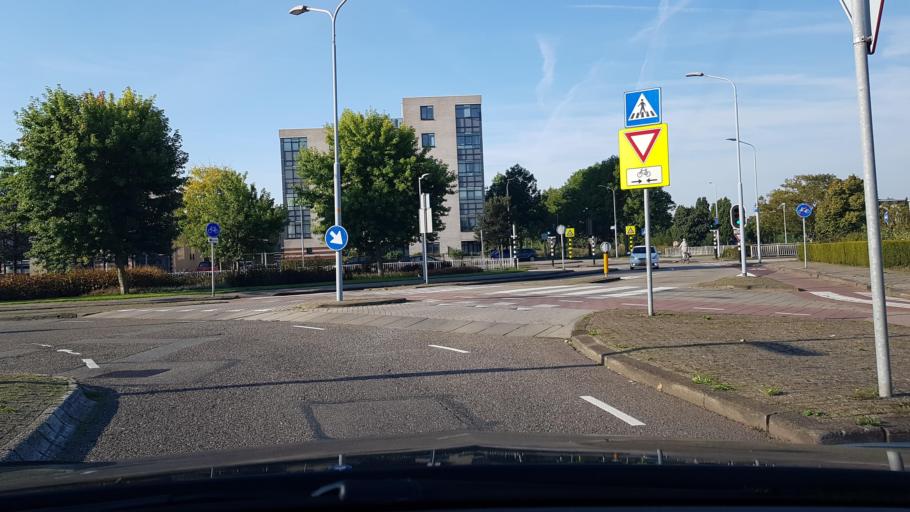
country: NL
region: North Holland
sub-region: Gemeente Haarlemmermeer
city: Hoofddorp
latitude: 52.3030
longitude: 4.6601
